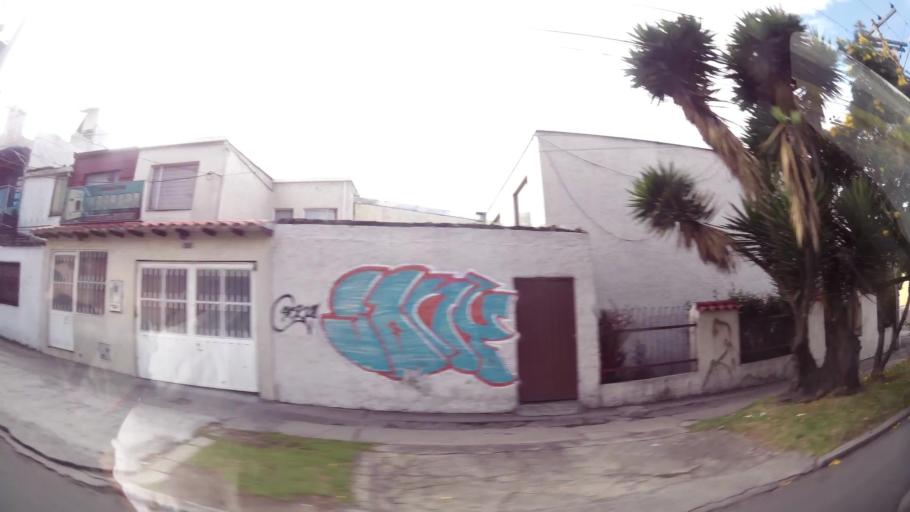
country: CO
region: Bogota D.C.
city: Barrio San Luis
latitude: 4.6915
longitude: -74.0790
